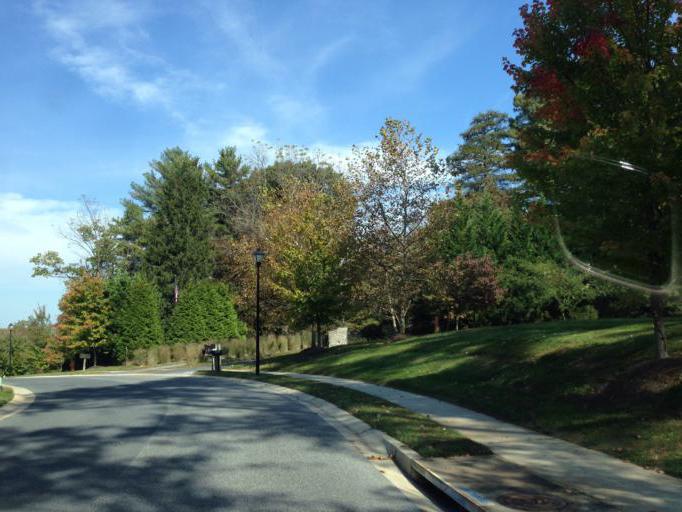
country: US
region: Maryland
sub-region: Howard County
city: Ellicott City
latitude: 39.2480
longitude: -76.8031
